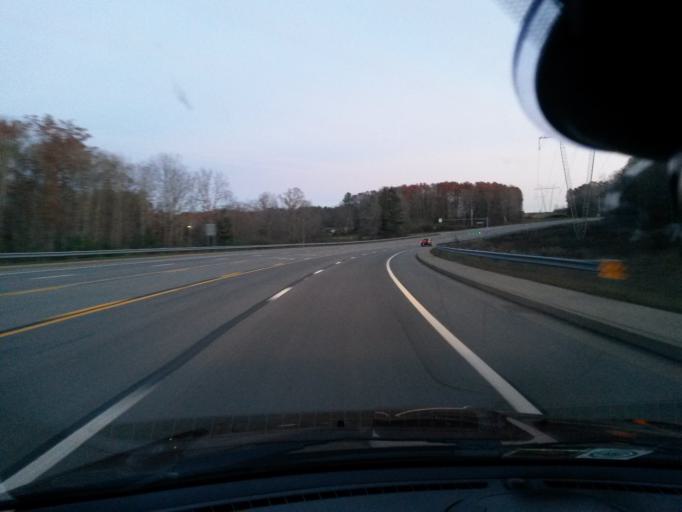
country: US
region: West Virginia
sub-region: Raleigh County
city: Stanaford
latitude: 37.7874
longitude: -81.1548
